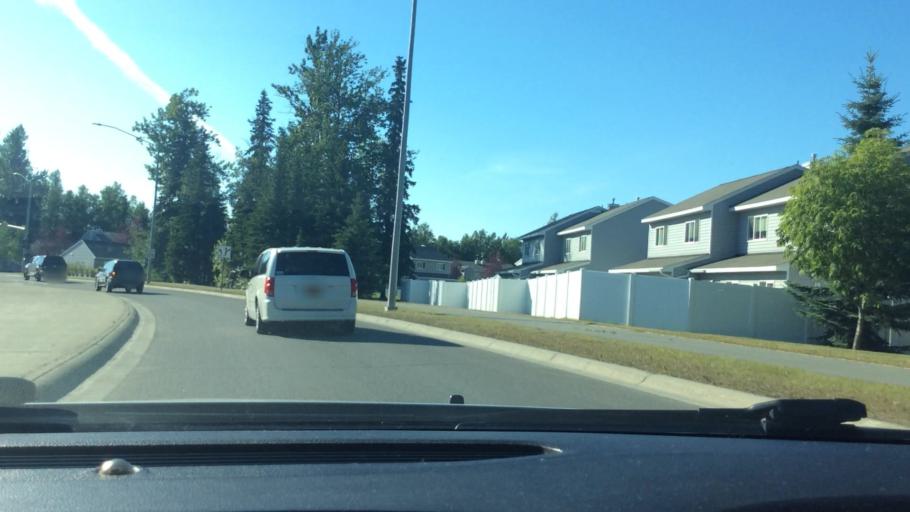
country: US
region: Alaska
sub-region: Anchorage Municipality
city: Anchorage
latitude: 61.2330
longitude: -149.7700
